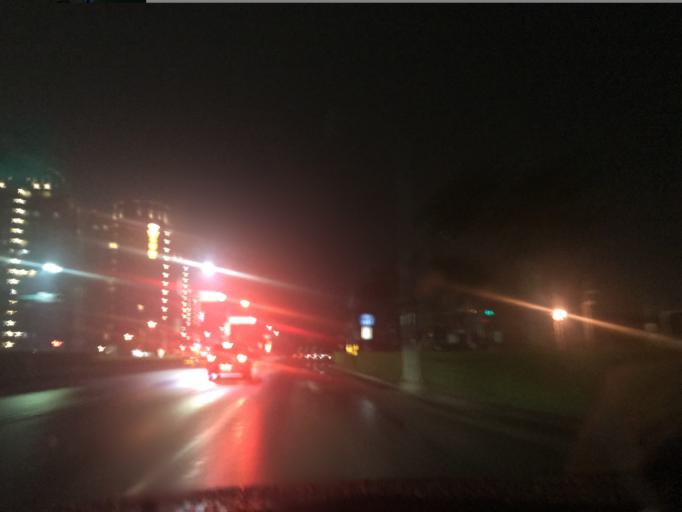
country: TW
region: Taiwan
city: Daxi
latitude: 24.9248
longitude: 121.2839
